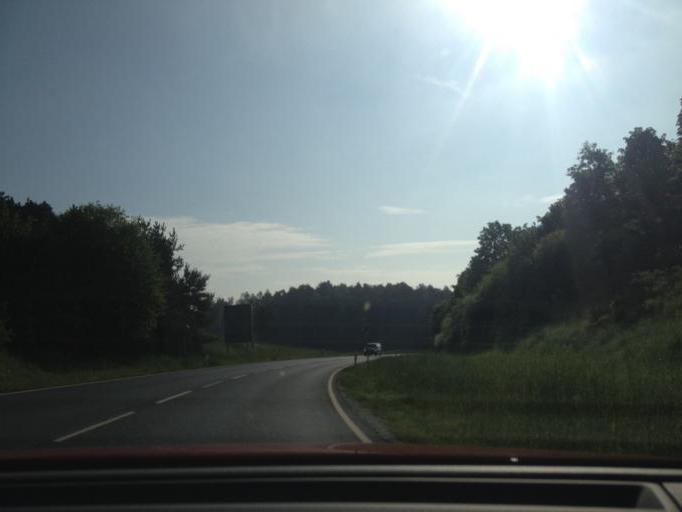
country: DE
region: Bavaria
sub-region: Upper Franconia
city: Pegnitz
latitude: 49.7413
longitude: 11.5155
